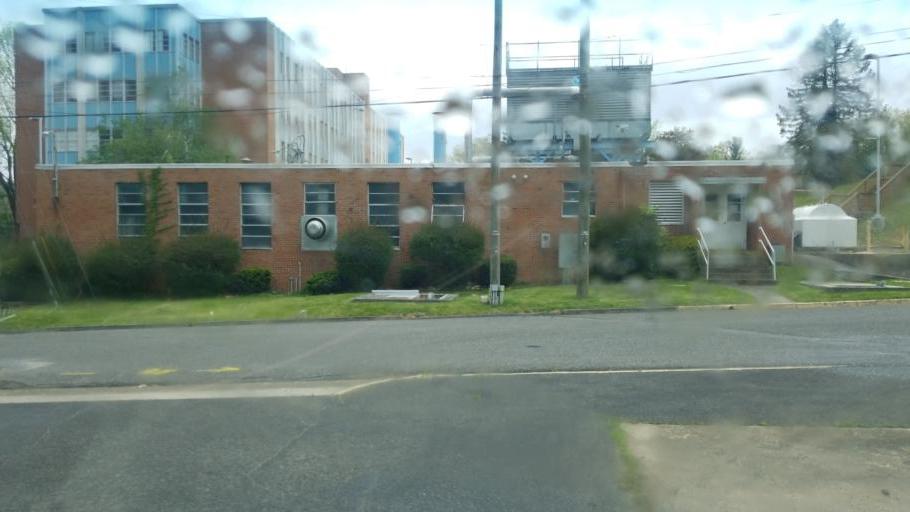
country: US
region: Virginia
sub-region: Smyth County
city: Marion
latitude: 36.8518
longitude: -81.5068
